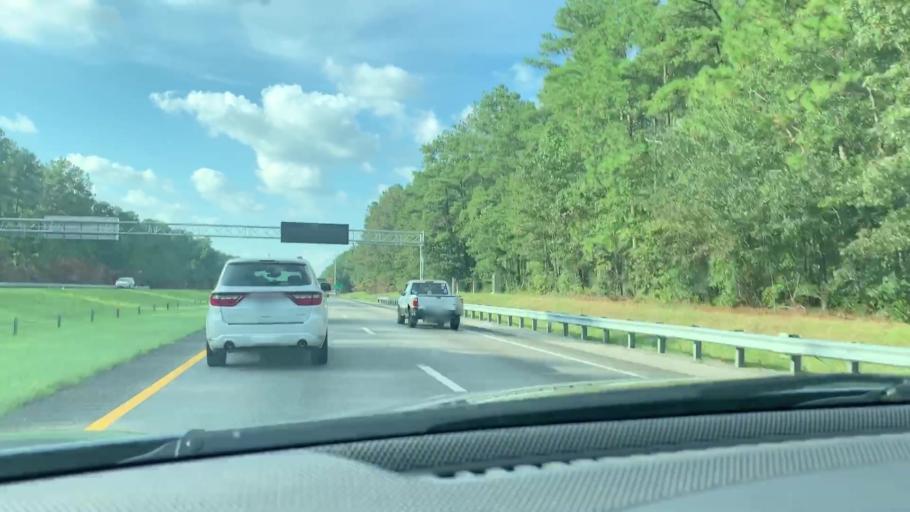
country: US
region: South Carolina
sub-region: Calhoun County
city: Oak Grove
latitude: 33.6807
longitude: -80.9033
